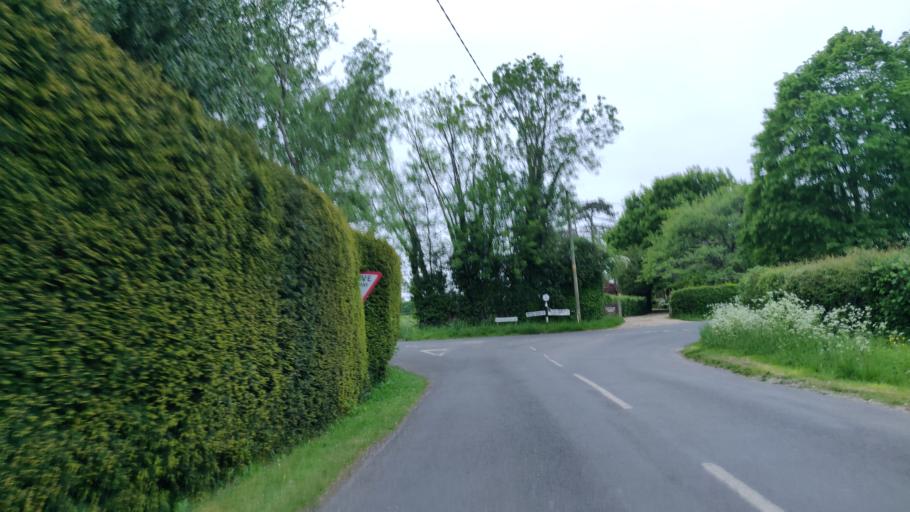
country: GB
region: England
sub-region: West Sussex
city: Southwater
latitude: 51.0269
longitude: -0.3684
